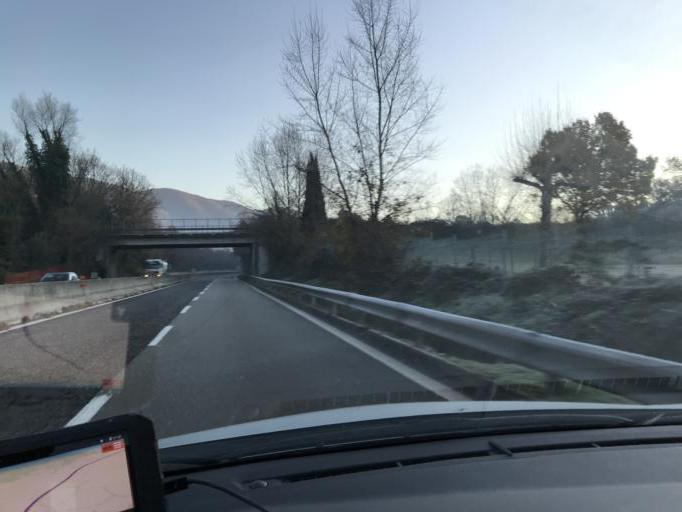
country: IT
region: Umbria
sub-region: Provincia di Terni
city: Terni
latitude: 42.5804
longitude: 12.6375
